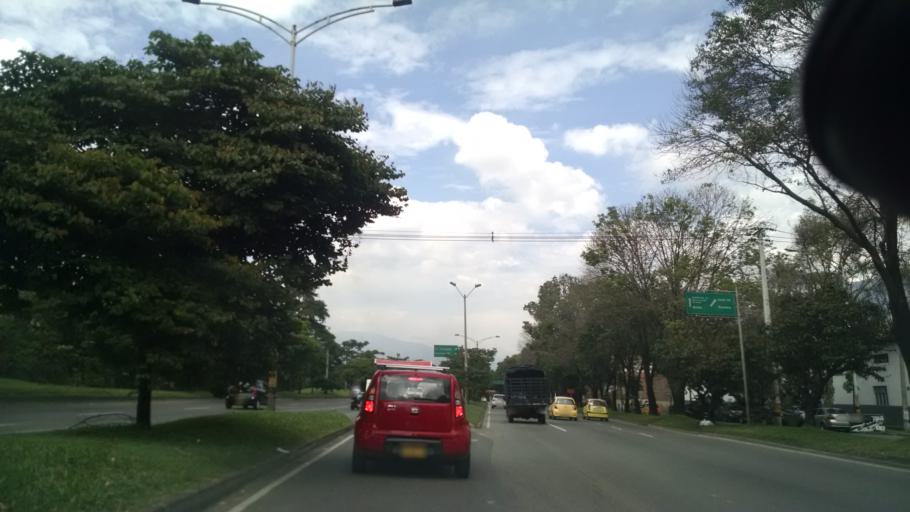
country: CO
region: Antioquia
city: Medellin
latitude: 6.2509
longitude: -75.5785
